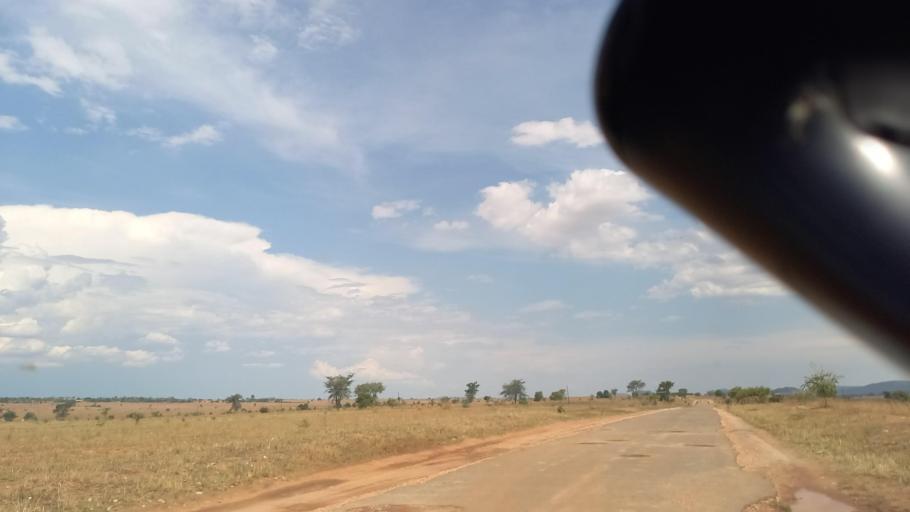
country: ZM
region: Lusaka
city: Kafue
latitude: -16.1942
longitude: 28.0961
